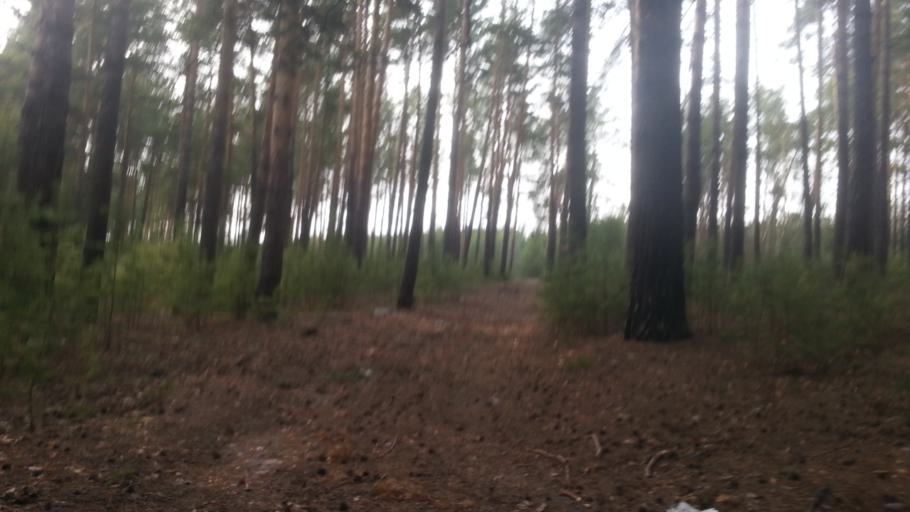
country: RU
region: Altai Krai
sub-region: Gorod Barnaulskiy
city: Barnaul
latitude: 53.3238
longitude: 83.7177
